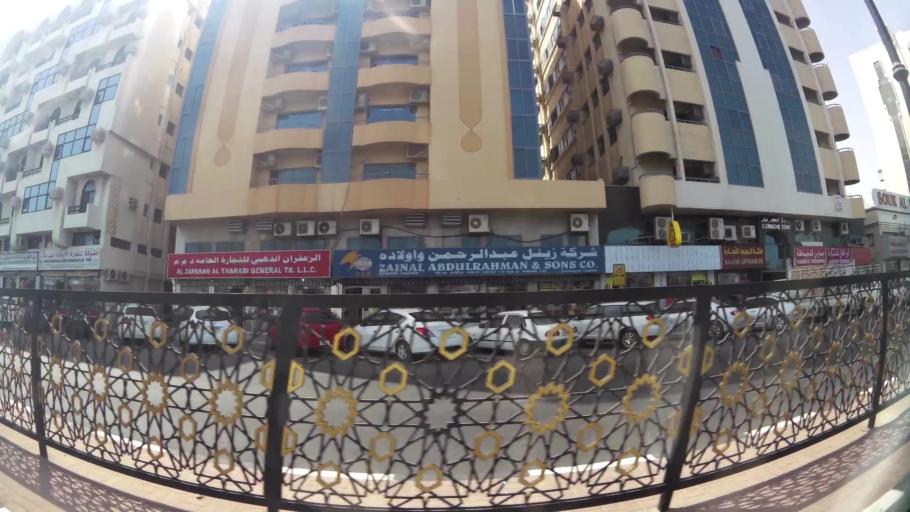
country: AE
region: Ash Shariqah
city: Sharjah
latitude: 25.3611
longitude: 55.3854
